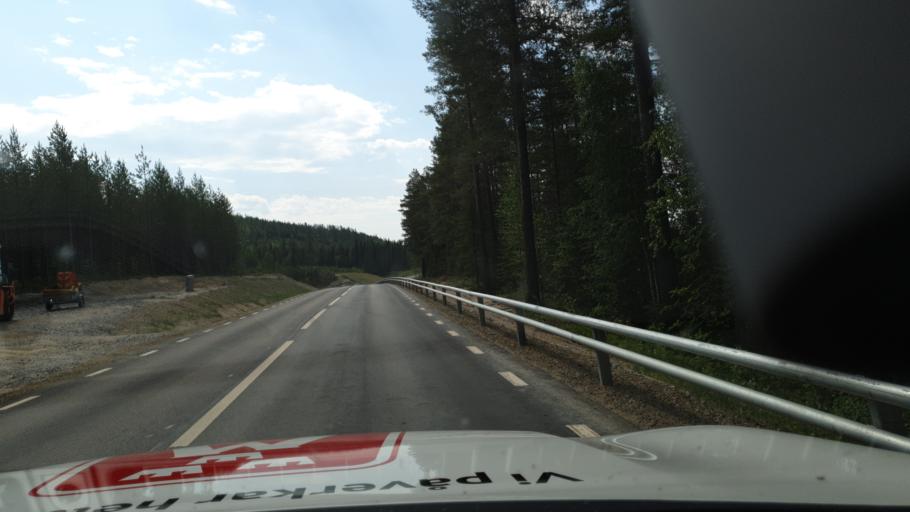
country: SE
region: Vaesterbotten
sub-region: Vindelns Kommun
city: Vindeln
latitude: 64.2682
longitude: 19.6340
